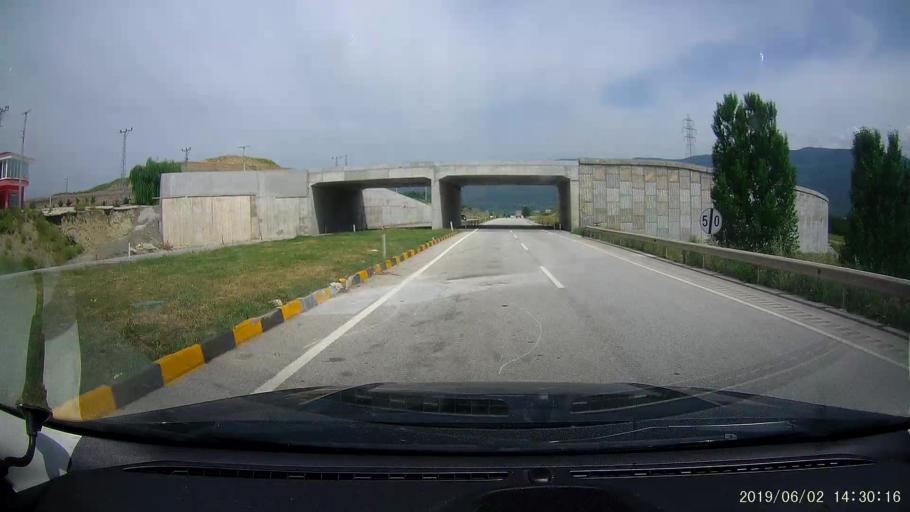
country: TR
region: Kastamonu
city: Tosya
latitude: 41.0187
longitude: 34.1111
